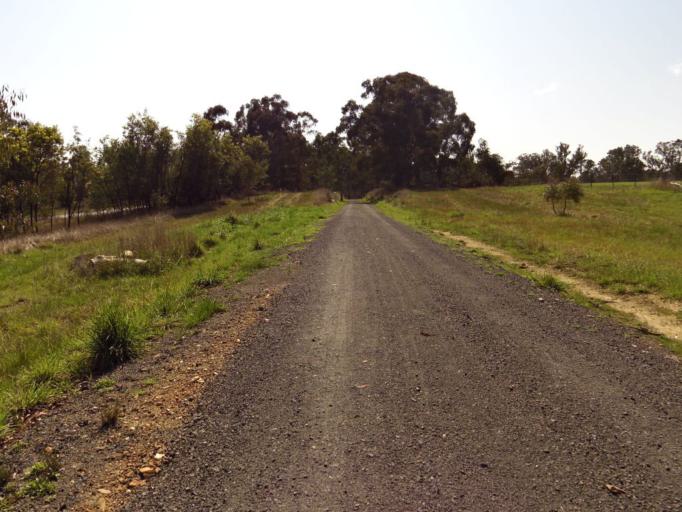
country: AU
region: Victoria
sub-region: Murrindindi
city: Alexandra
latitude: -37.1212
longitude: 145.6020
